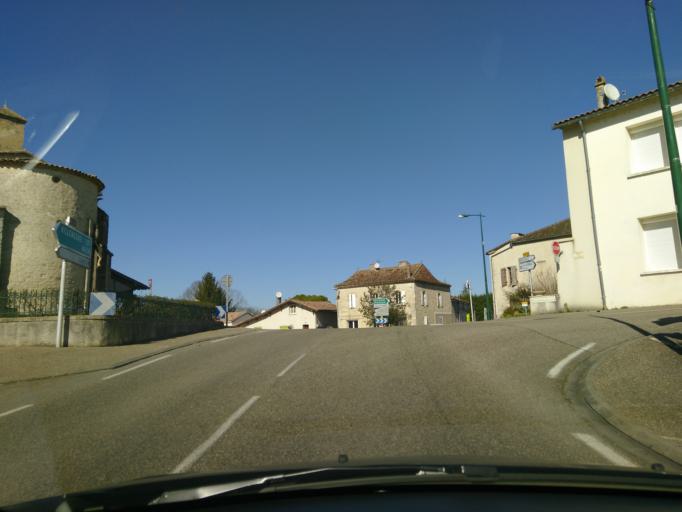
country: FR
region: Aquitaine
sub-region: Departement du Lot-et-Garonne
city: Cancon
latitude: 44.5829
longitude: 0.6232
